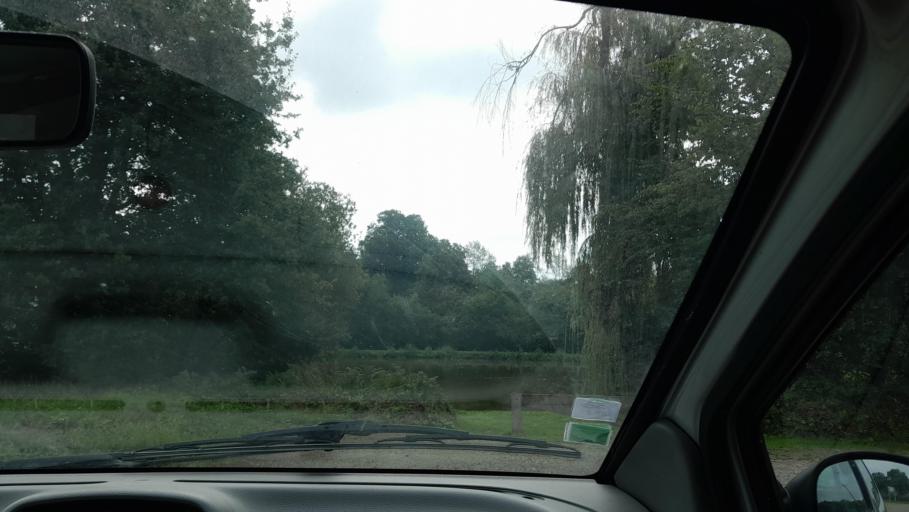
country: FR
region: Pays de la Loire
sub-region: Departement de la Mayenne
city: Cosse-le-Vivien
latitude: 47.9493
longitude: -0.9185
